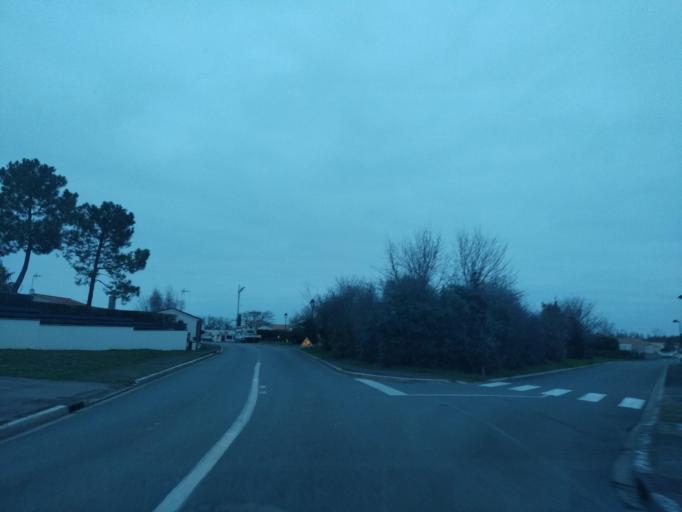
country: FR
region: Pays de la Loire
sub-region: Departement de la Vendee
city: Triaize
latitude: 46.3598
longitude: -1.2494
